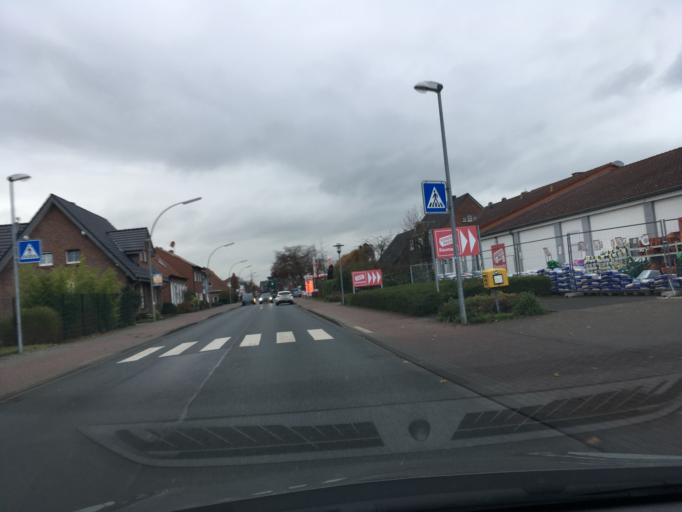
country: DE
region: North Rhine-Westphalia
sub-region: Regierungsbezirk Munster
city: Ahaus
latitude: 52.0911
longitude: 6.9786
